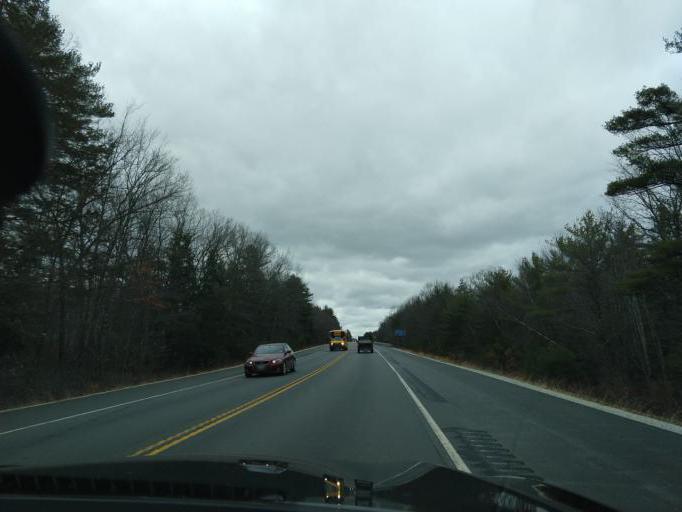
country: US
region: New Hampshire
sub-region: Rockingham County
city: Kingston
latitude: 42.9244
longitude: -71.0455
